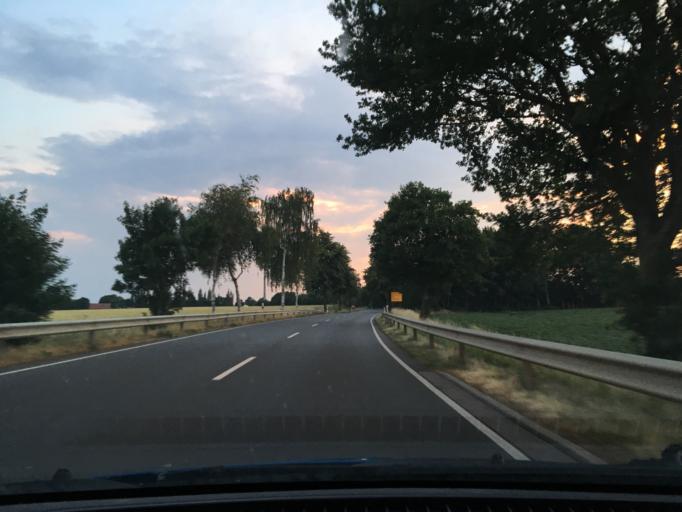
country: DE
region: Lower Saxony
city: Bad Bevensen
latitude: 53.0699
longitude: 10.5761
